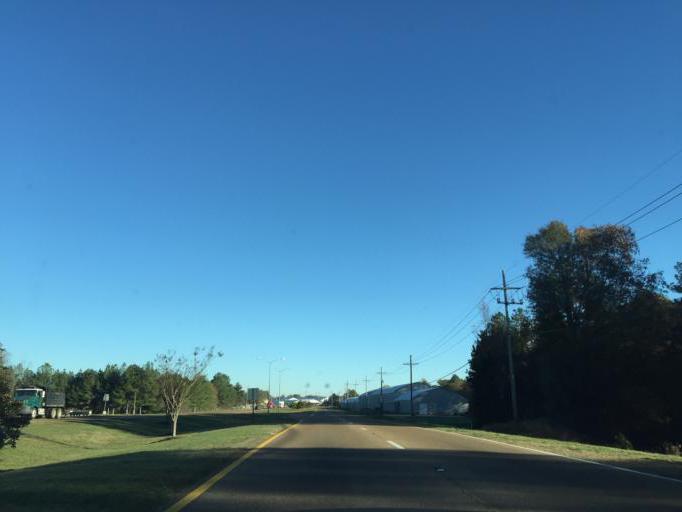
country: US
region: Mississippi
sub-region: Rankin County
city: Flowood
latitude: 32.2969
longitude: -90.1438
